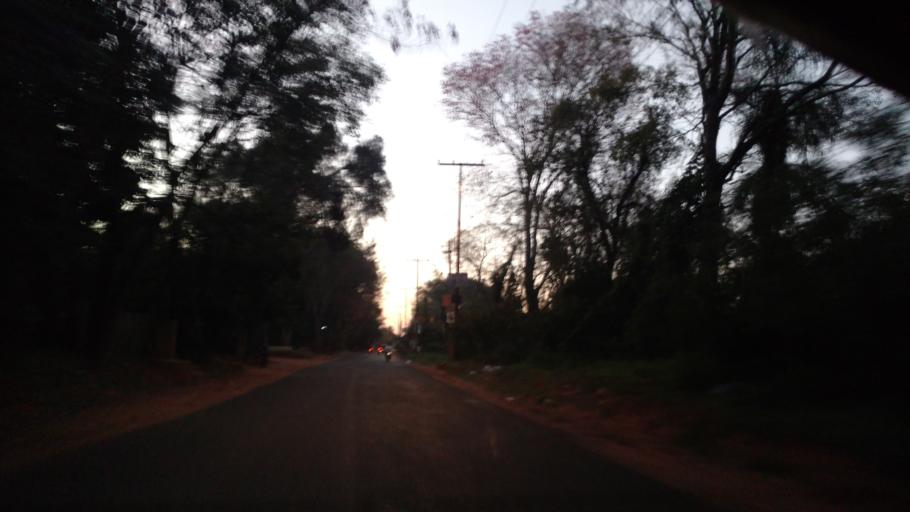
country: PY
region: Central
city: Capiata
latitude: -25.3973
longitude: -57.4097
